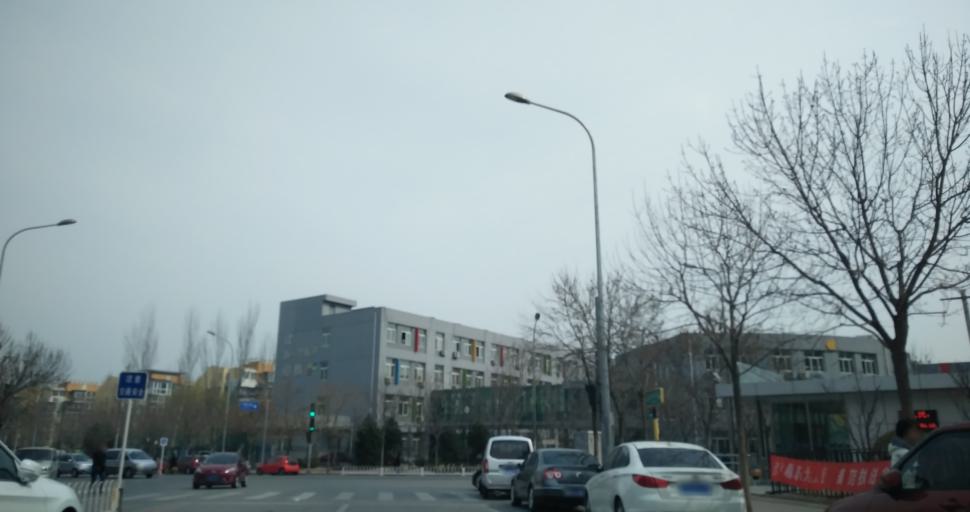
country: CN
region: Beijing
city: Jiugong
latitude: 39.8561
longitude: 116.4989
